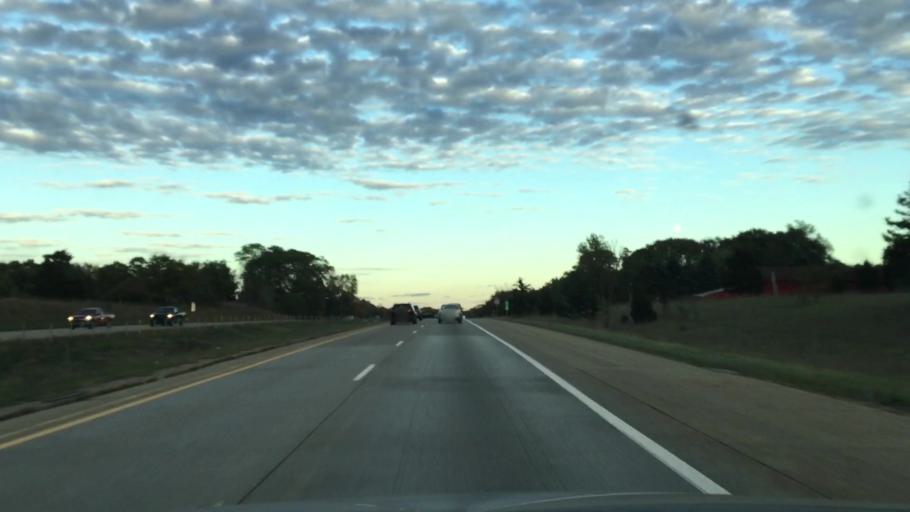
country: US
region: Michigan
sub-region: Jackson County
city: Grass Lake
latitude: 42.2918
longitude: -84.2470
